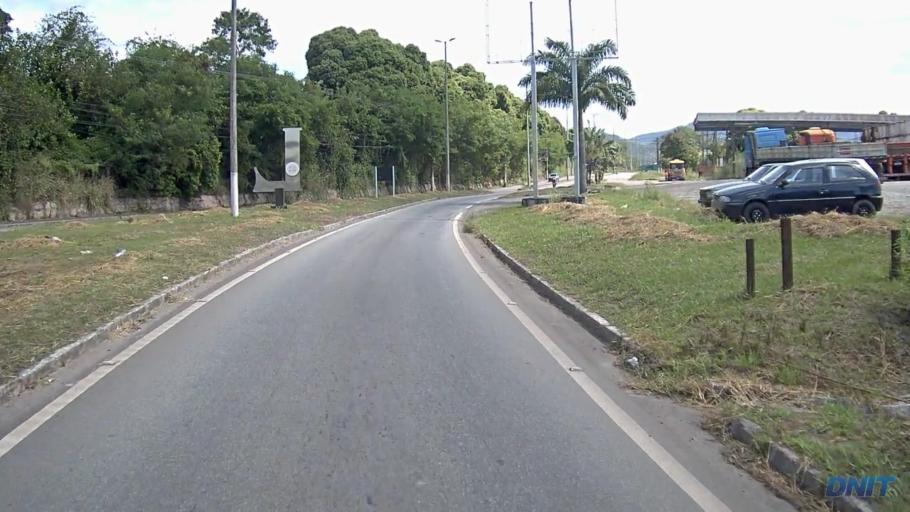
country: BR
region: Minas Gerais
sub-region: Coronel Fabriciano
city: Coronel Fabriciano
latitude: -19.5277
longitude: -42.6417
